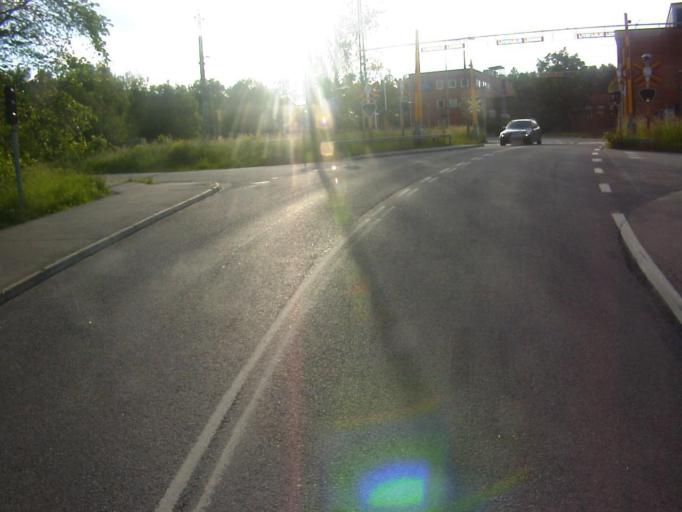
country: SE
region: Soedermanland
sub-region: Eskilstuna Kommun
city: Skogstorp
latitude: 59.3321
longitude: 16.4752
